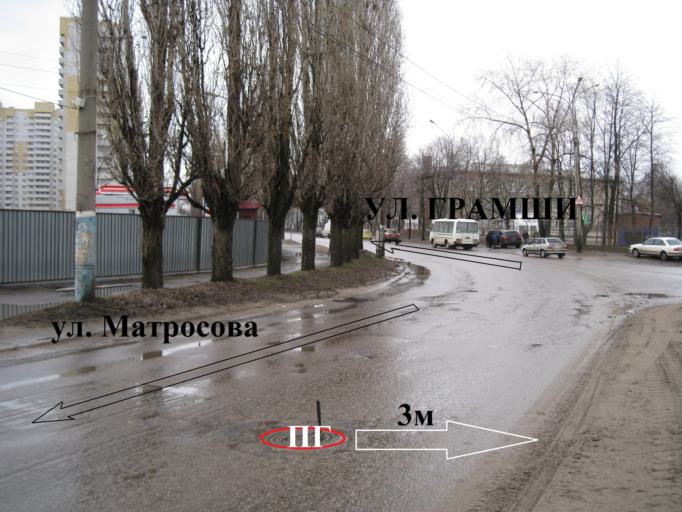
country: RU
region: Voronezj
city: Voronezh
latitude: 51.6327
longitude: 39.1810
